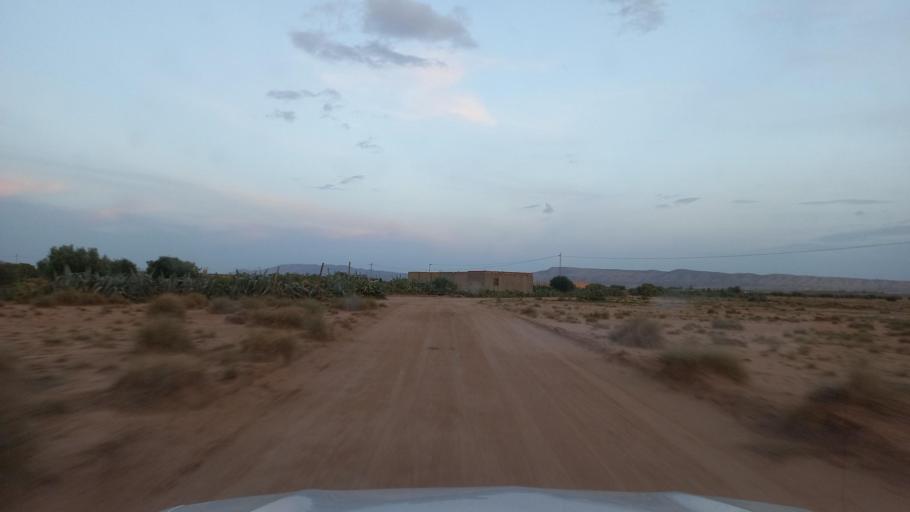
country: TN
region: Al Qasrayn
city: Sbiba
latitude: 35.3499
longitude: 9.0421
